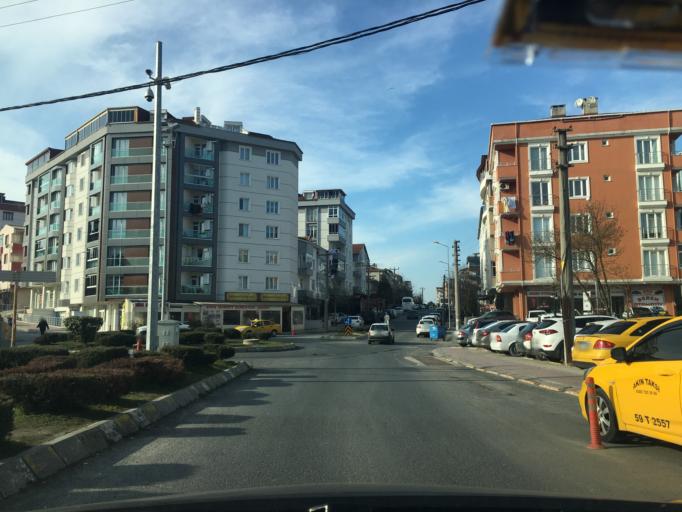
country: TR
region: Tekirdag
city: Cerkezkoey
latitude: 41.2900
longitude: 27.9970
